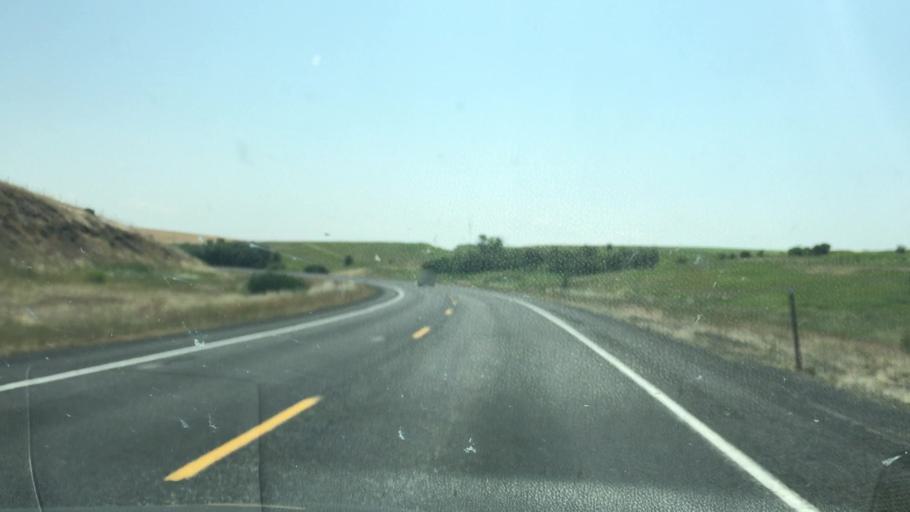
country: US
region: Idaho
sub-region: Lewis County
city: Nezperce
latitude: 46.2216
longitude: -116.4365
